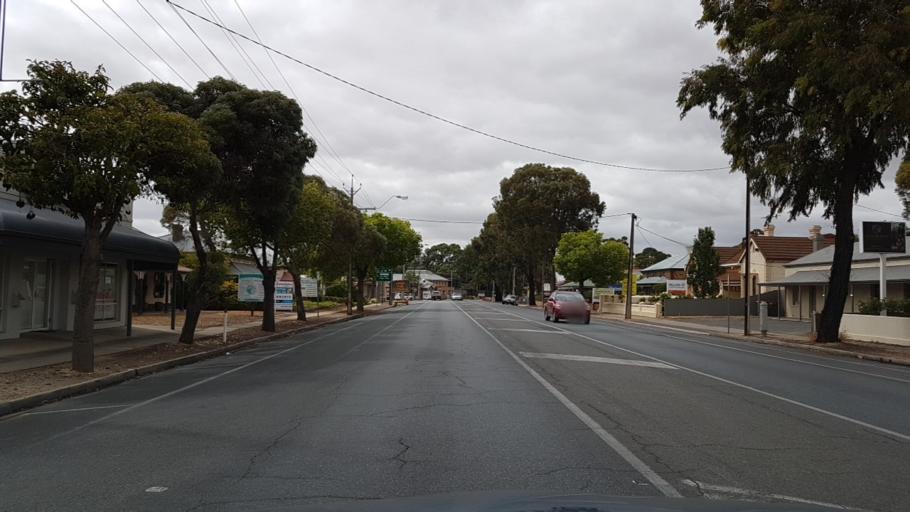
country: AU
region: South Australia
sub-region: Gawler
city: Gawler
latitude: -34.6056
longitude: 138.7447
